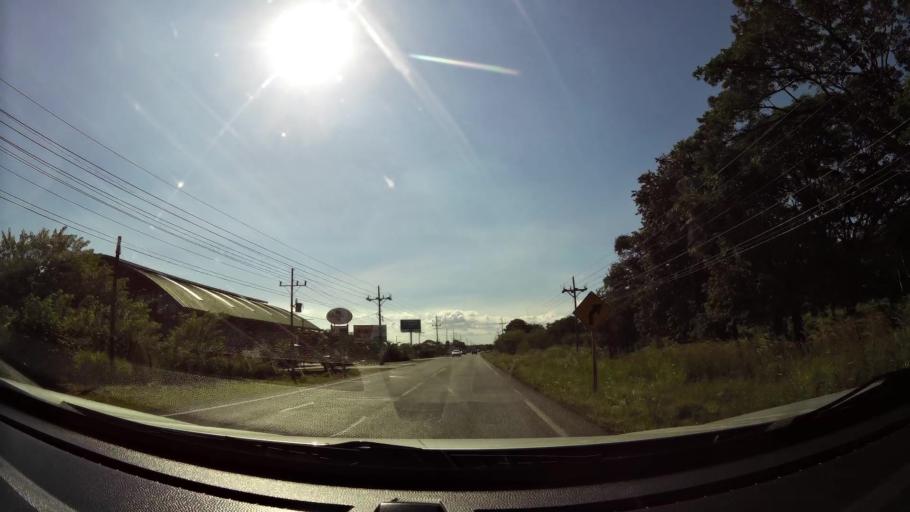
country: CR
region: Guanacaste
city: Liberia
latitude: 10.6179
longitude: -85.4649
